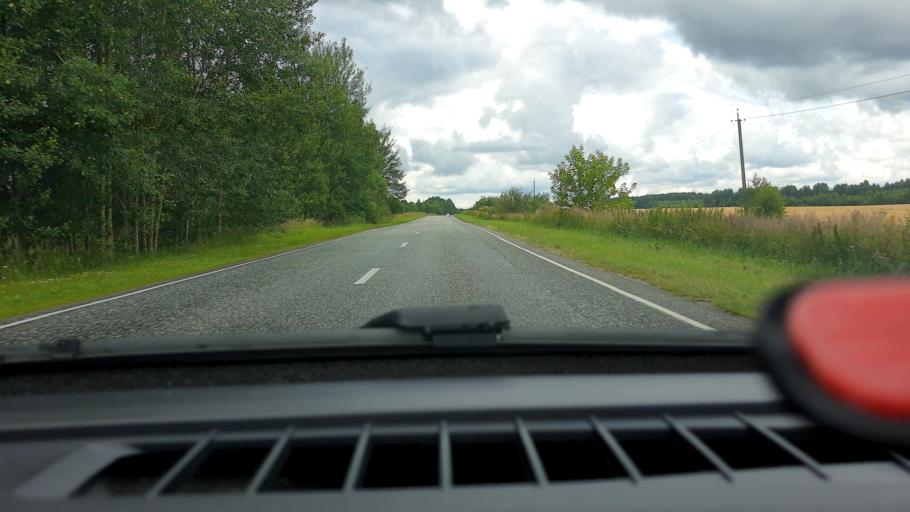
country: RU
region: Nizjnij Novgorod
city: Neklyudovo
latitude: 56.5188
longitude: 43.9042
